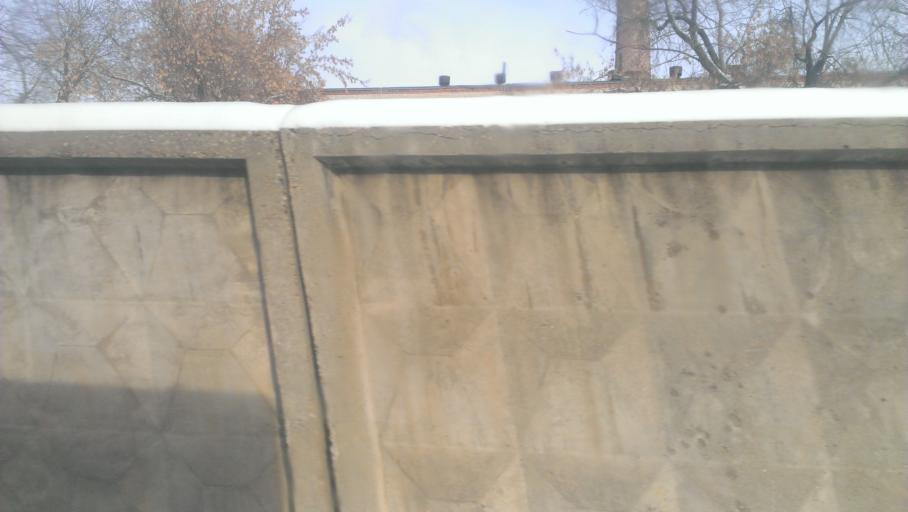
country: RU
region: Altai Krai
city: Nauchnyy Gorodok
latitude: 53.4218
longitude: 83.5207
